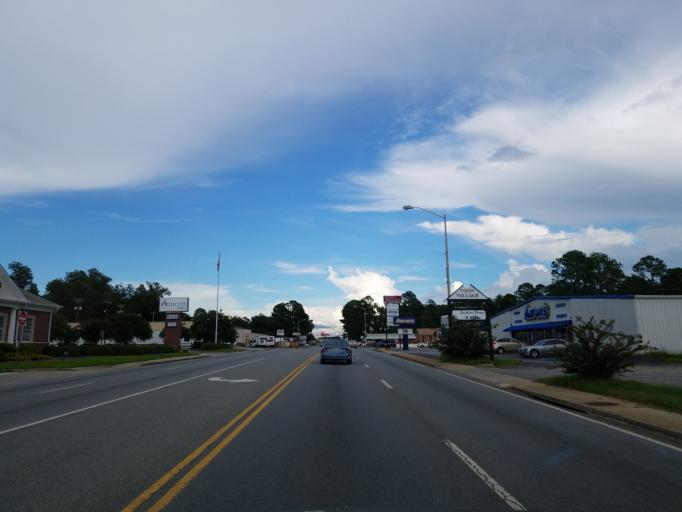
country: US
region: Georgia
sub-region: Crisp County
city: Cordele
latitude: 31.9636
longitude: -83.7759
